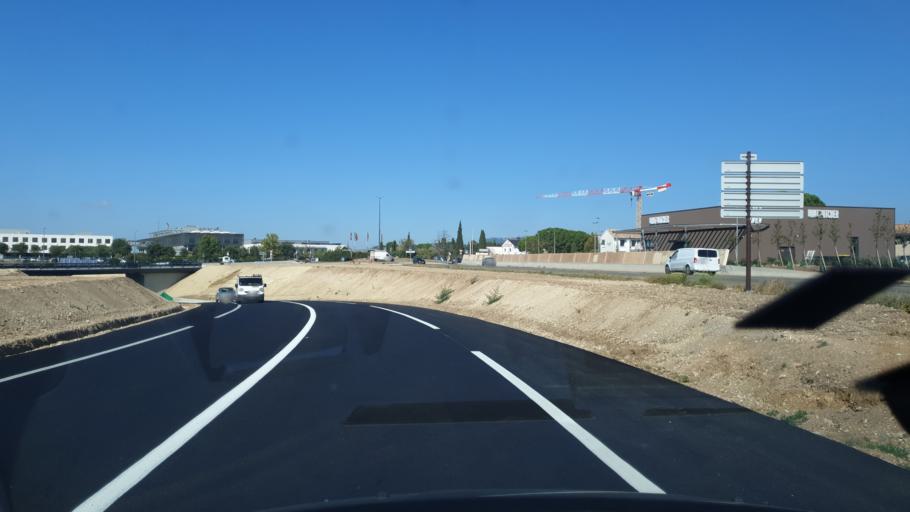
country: FR
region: Provence-Alpes-Cote d'Azur
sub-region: Departement du Vaucluse
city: Carpentras
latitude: 44.0442
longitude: 5.0298
